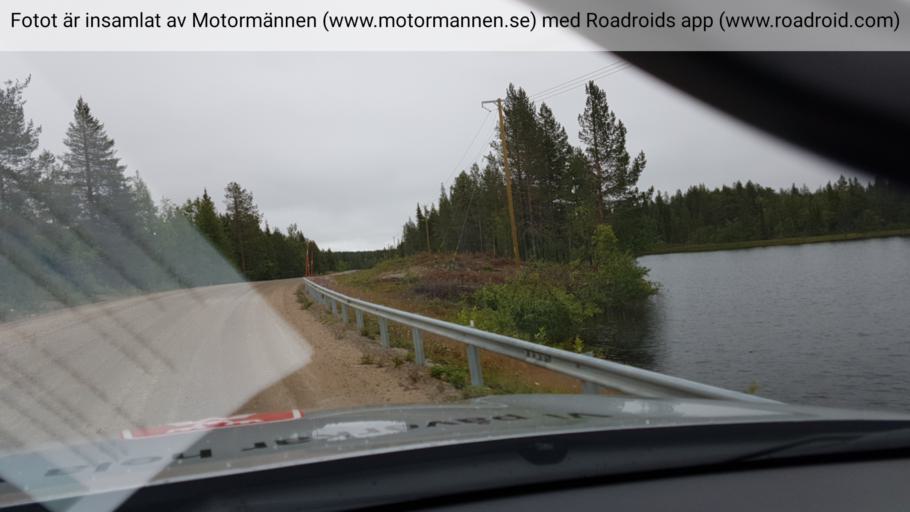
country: SE
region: Norrbotten
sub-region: Gallivare Kommun
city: Gaellivare
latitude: 66.7467
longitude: 20.6260
